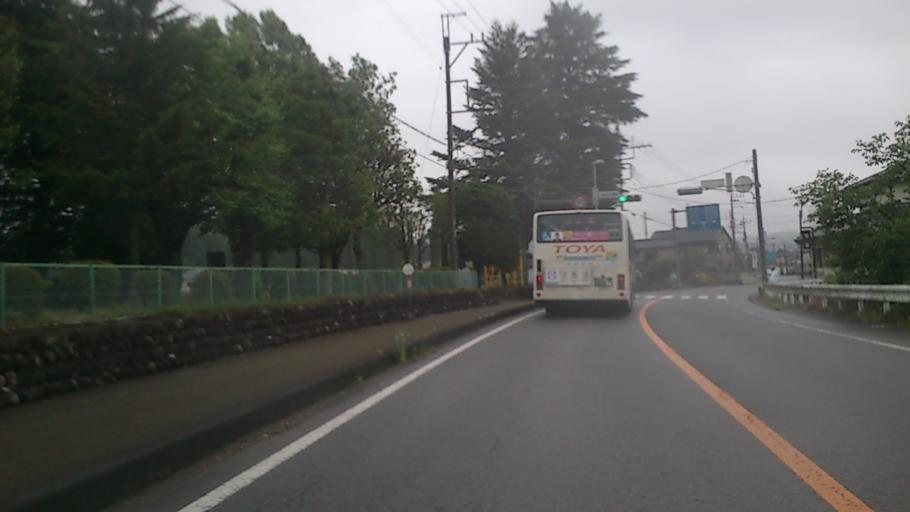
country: JP
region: Tochigi
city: Otawara
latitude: 36.7922
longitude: 140.1185
